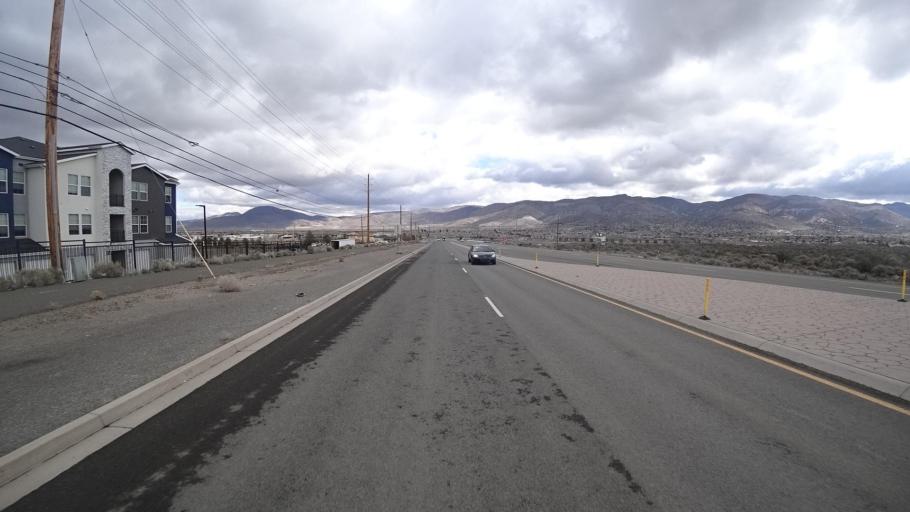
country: US
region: Nevada
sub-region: Washoe County
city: Sparks
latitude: 39.3993
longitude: -119.7530
